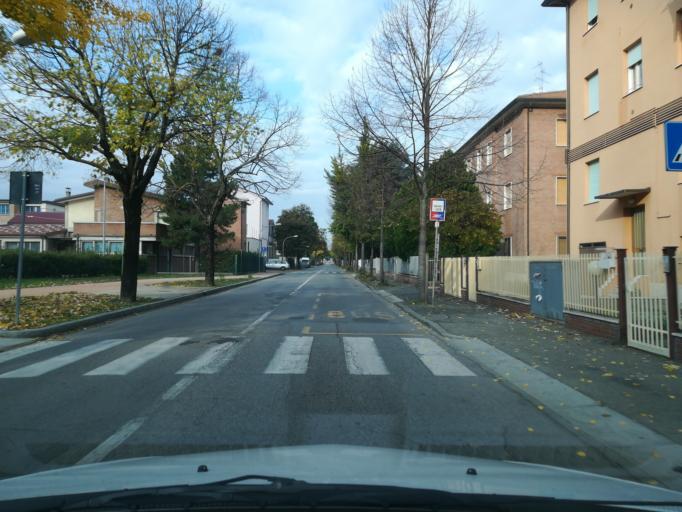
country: IT
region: Emilia-Romagna
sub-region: Provincia di Bologna
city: Imola
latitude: 44.3624
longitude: 11.7201
